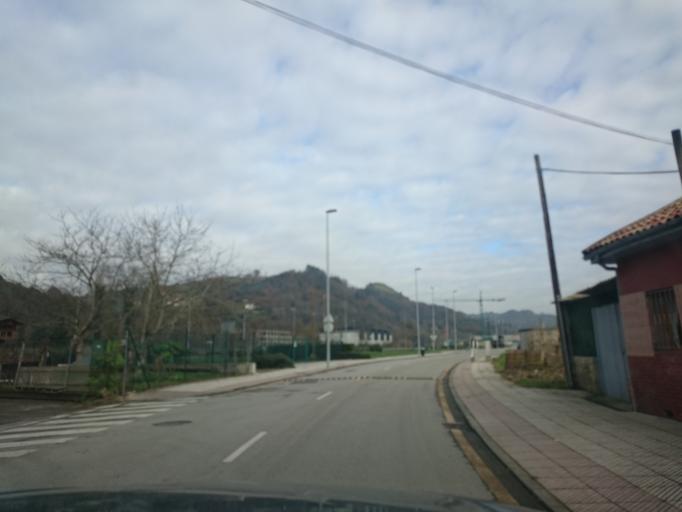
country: ES
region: Asturias
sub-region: Province of Asturias
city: Oviedo
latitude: 43.3211
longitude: -5.8010
